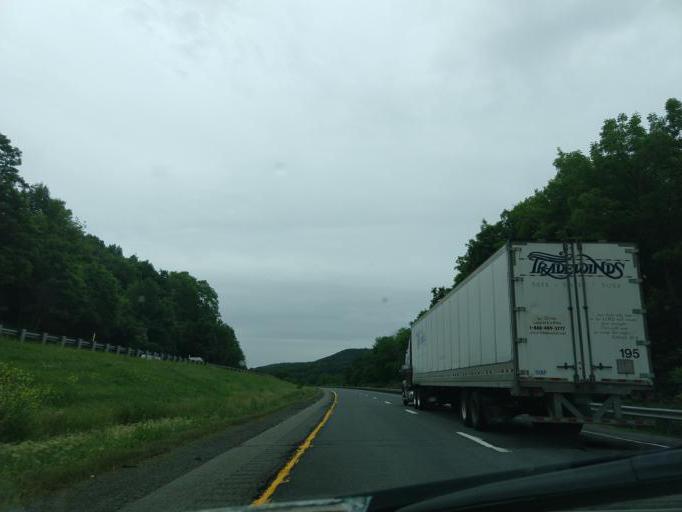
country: US
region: Pennsylvania
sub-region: Susquehanna County
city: Hallstead
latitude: 41.9562
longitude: -75.7380
